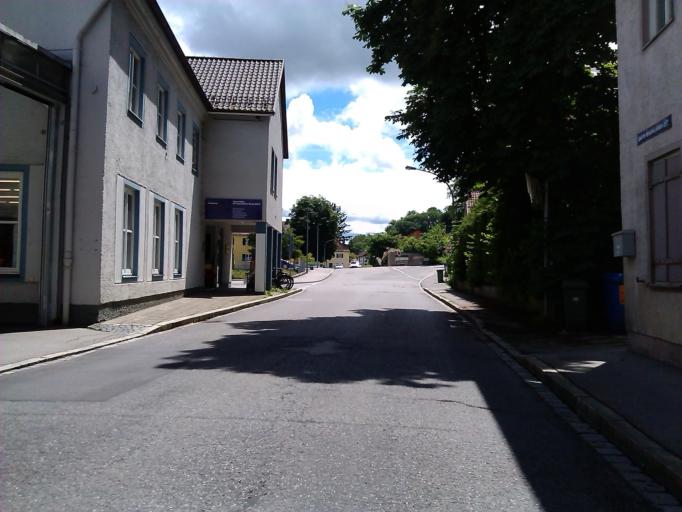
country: DE
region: Bavaria
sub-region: Swabia
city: Kaufbeuren
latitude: 47.8764
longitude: 10.6208
